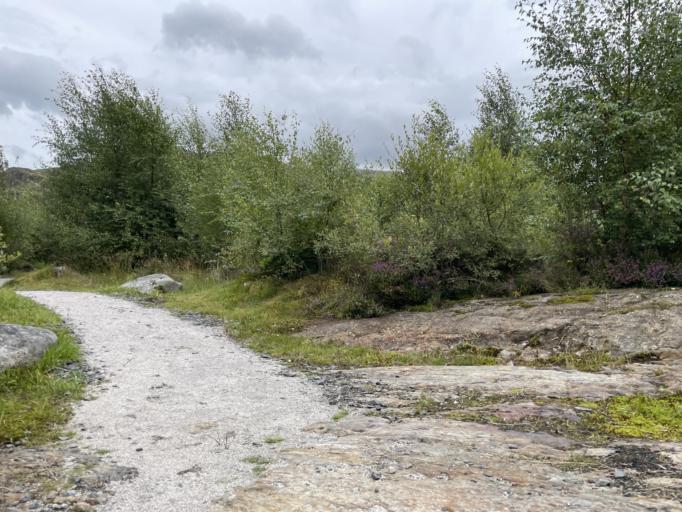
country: GB
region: Scotland
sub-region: Dumfries and Galloway
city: Newton Stewart
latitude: 55.0859
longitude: -4.5027
